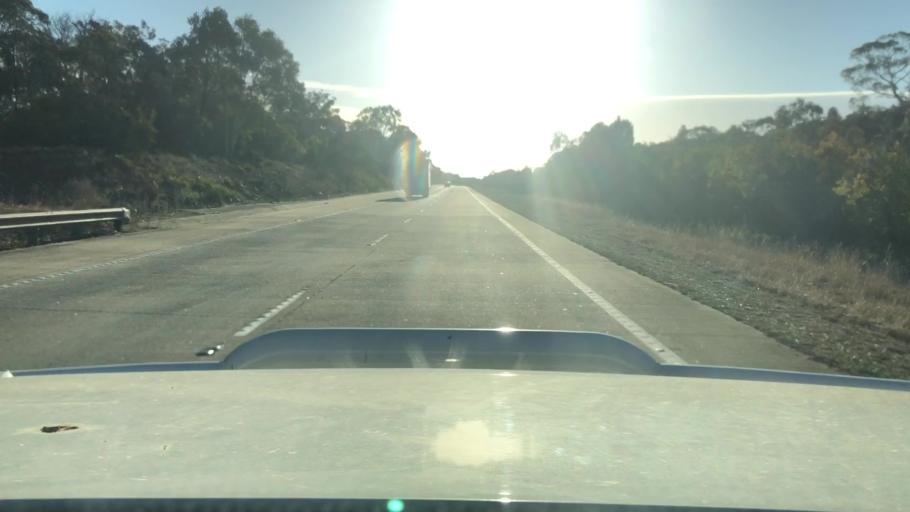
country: AU
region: New South Wales
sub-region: Wingecarribee
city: Moss Vale
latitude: -34.4736
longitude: 150.3248
